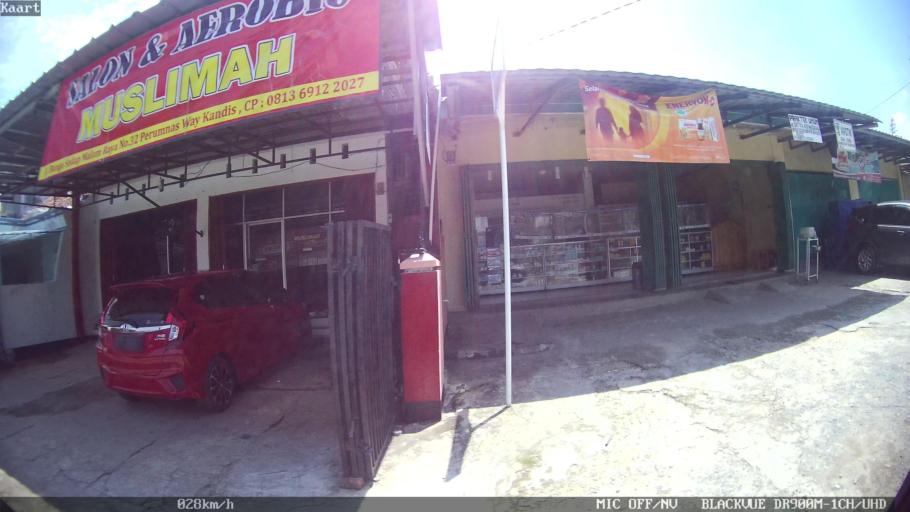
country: ID
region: Lampung
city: Kedaton
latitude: -5.3629
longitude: 105.2872
